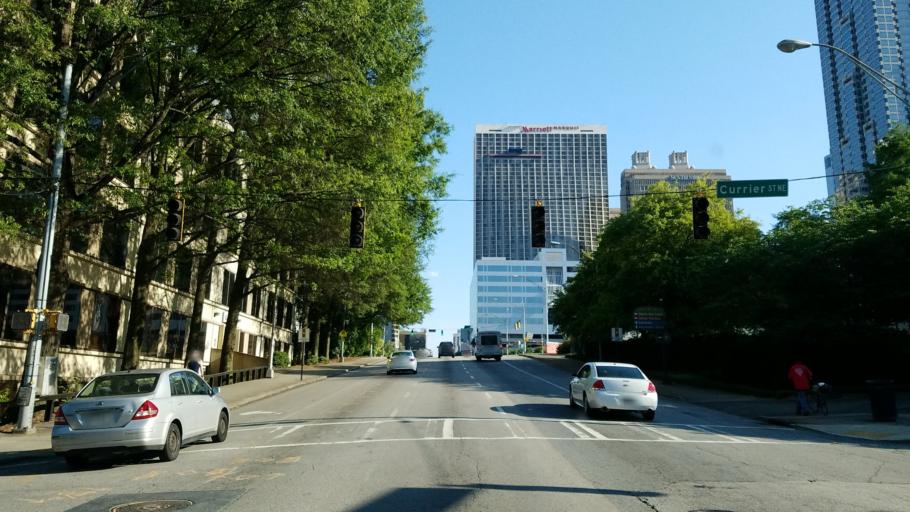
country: US
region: Georgia
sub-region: Fulton County
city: Atlanta
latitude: 33.7656
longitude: -84.3841
